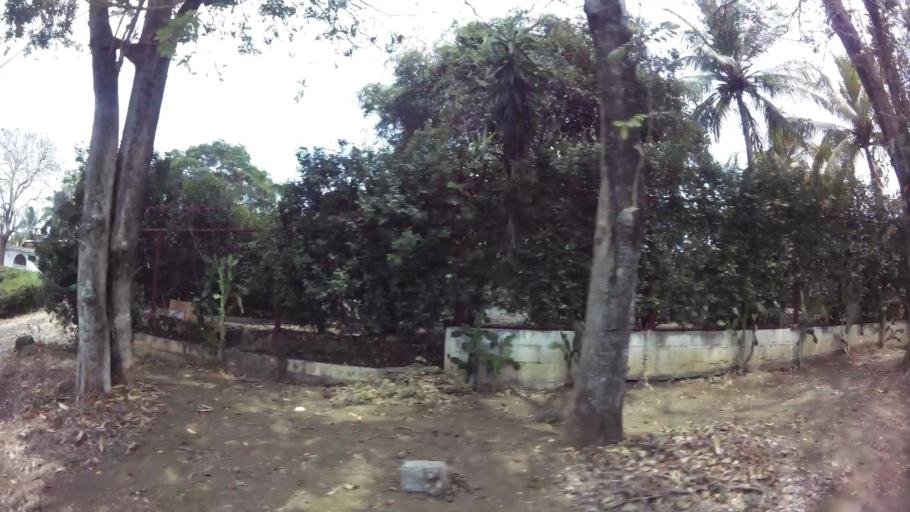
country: NI
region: Managua
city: Managua
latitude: 12.0972
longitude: -86.2276
